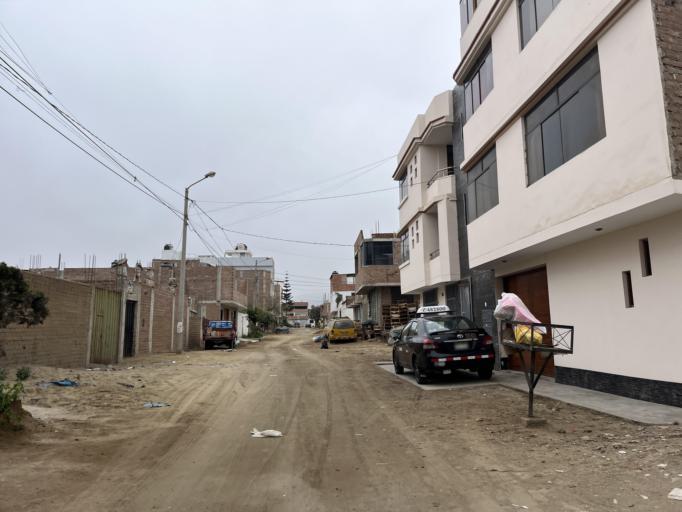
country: PE
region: La Libertad
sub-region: Provincia de Trujillo
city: La Esperanza
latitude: -8.0883
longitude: -79.0518
